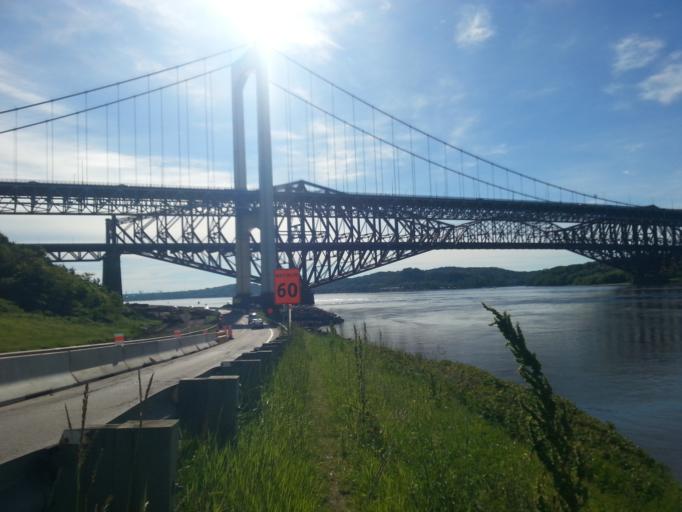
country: CA
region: Quebec
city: L'Ancienne-Lorette
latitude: 46.7482
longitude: -71.2959
